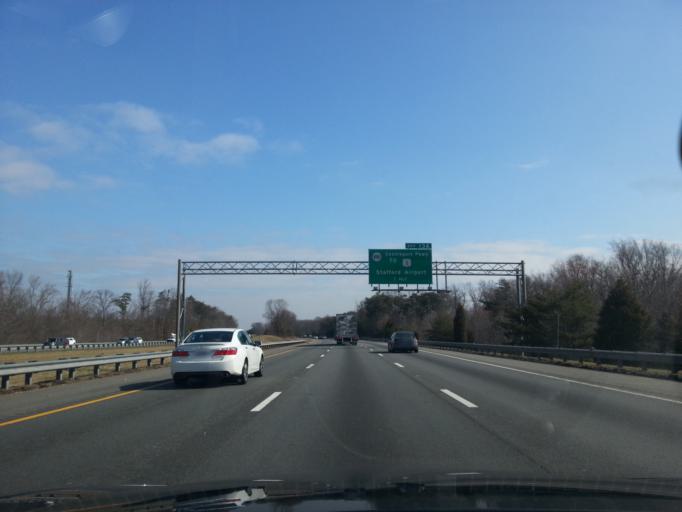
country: US
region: Virginia
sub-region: Stafford County
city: Falmouth
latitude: 38.3563
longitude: -77.4738
